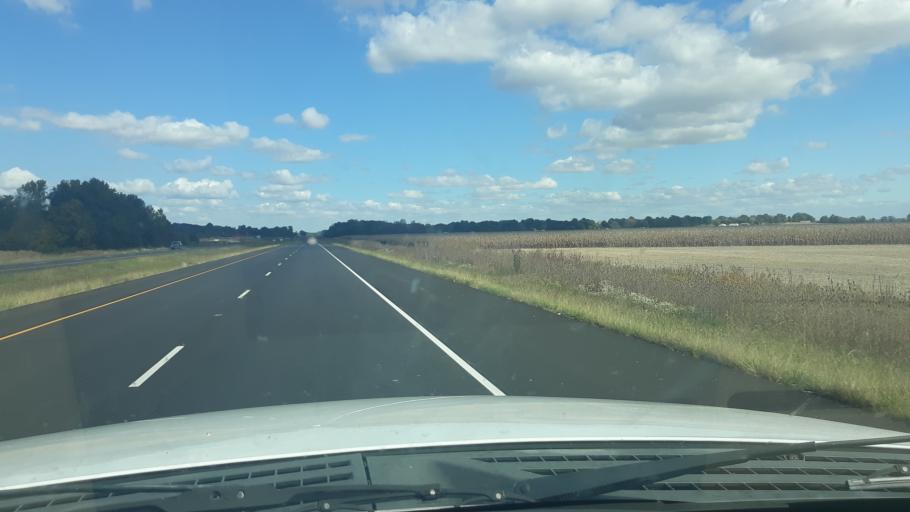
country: US
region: Illinois
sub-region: Saline County
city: Harrisburg
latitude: 37.7778
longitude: -88.4998
